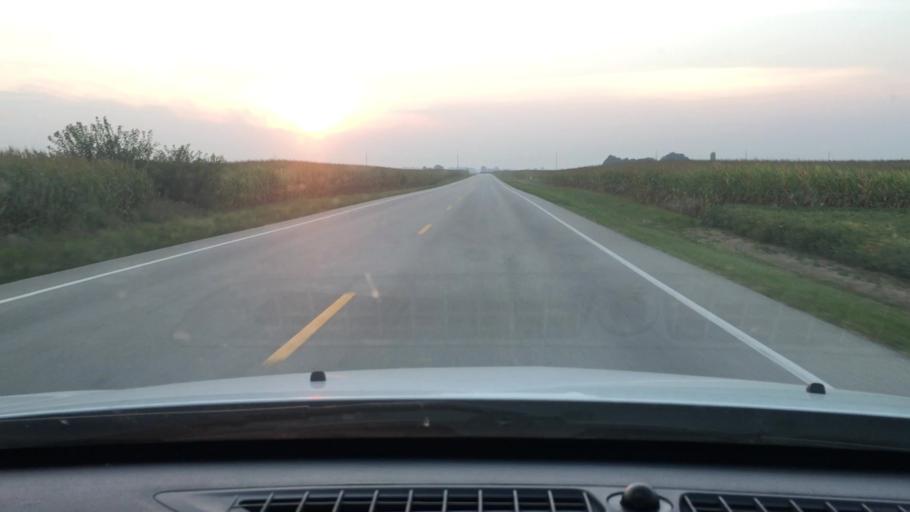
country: US
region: Illinois
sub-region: DeKalb County
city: Malta
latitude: 41.8486
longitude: -88.8383
